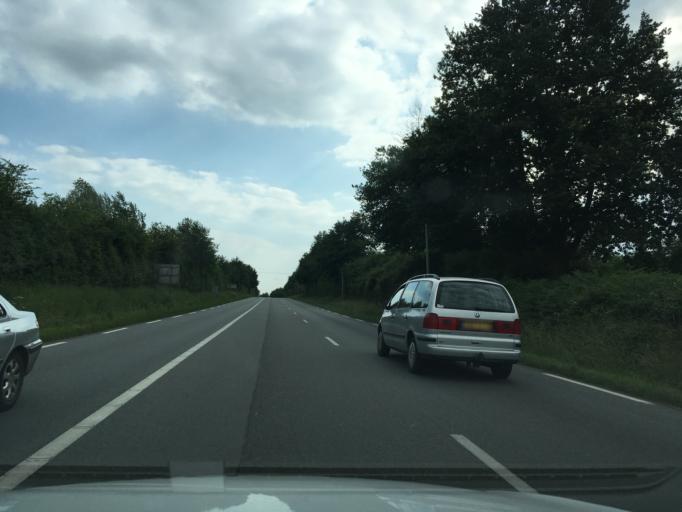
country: FR
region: Poitou-Charentes
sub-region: Departement des Deux-Sevres
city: Le Tallud
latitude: 46.6277
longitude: -0.2755
